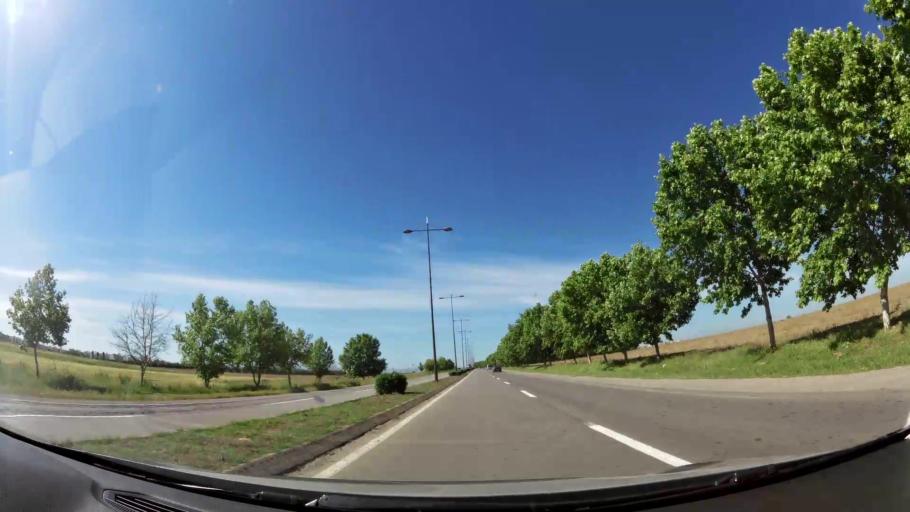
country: MA
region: Fes-Boulemane
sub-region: Fes
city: Fes
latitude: 34.0026
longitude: -5.0233
